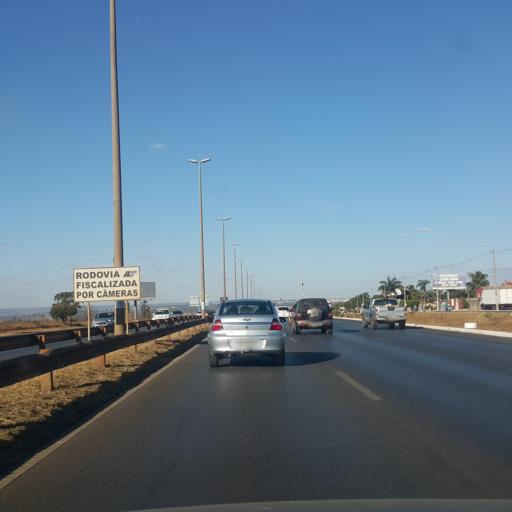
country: BR
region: Federal District
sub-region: Brasilia
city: Brasilia
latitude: -15.7912
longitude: -48.0465
